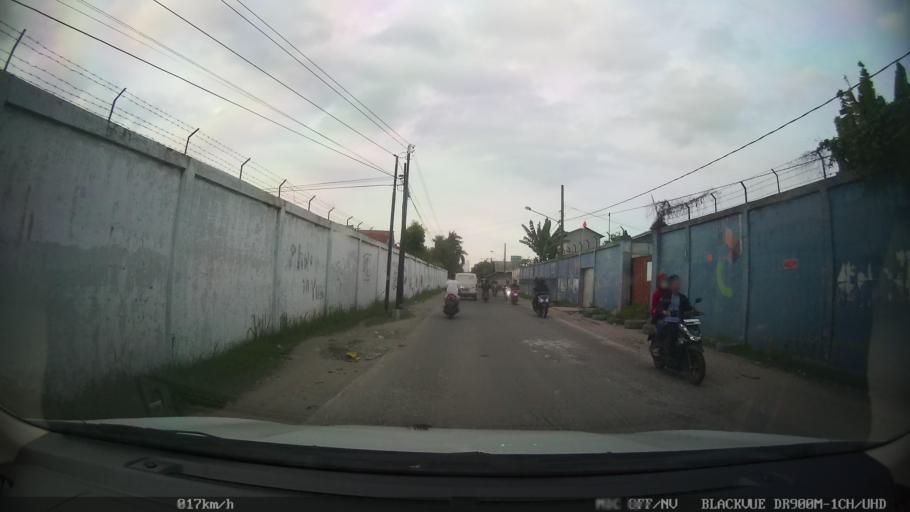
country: ID
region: North Sumatra
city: Sunggal
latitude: 3.5675
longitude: 98.6113
